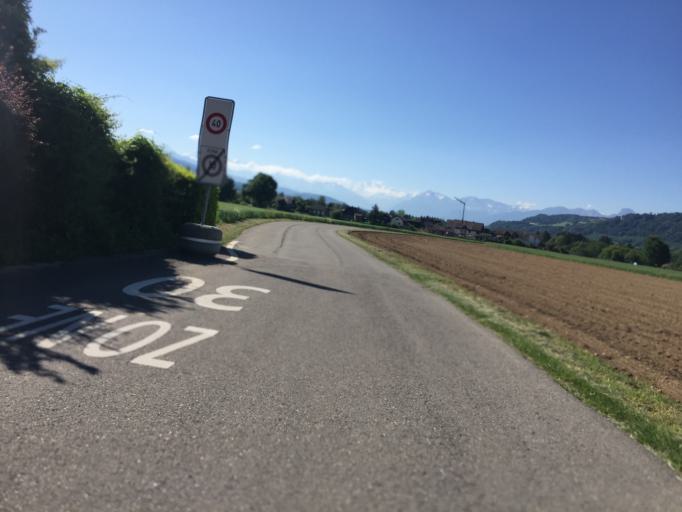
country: CH
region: Bern
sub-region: Bern-Mittelland District
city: Rubigen
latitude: 46.8985
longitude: 7.5382
